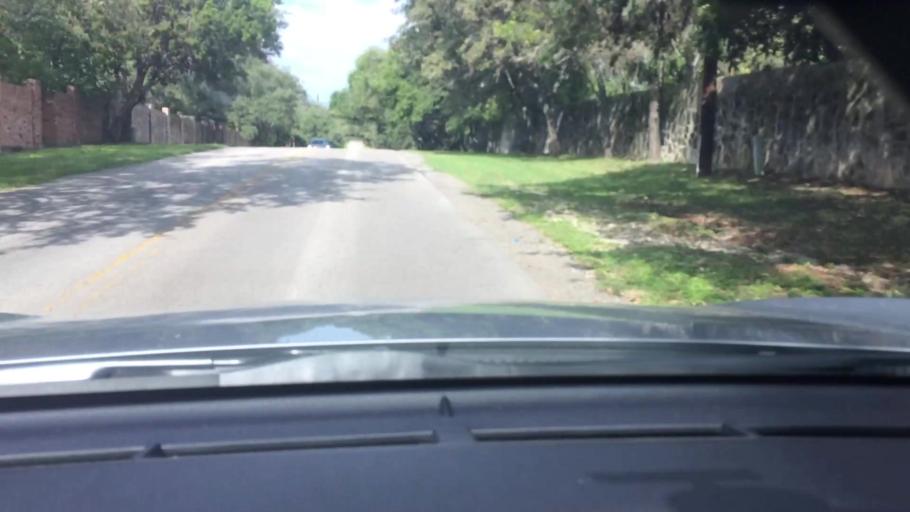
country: US
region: Texas
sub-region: Bexar County
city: Shavano Park
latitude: 29.5568
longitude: -98.5597
